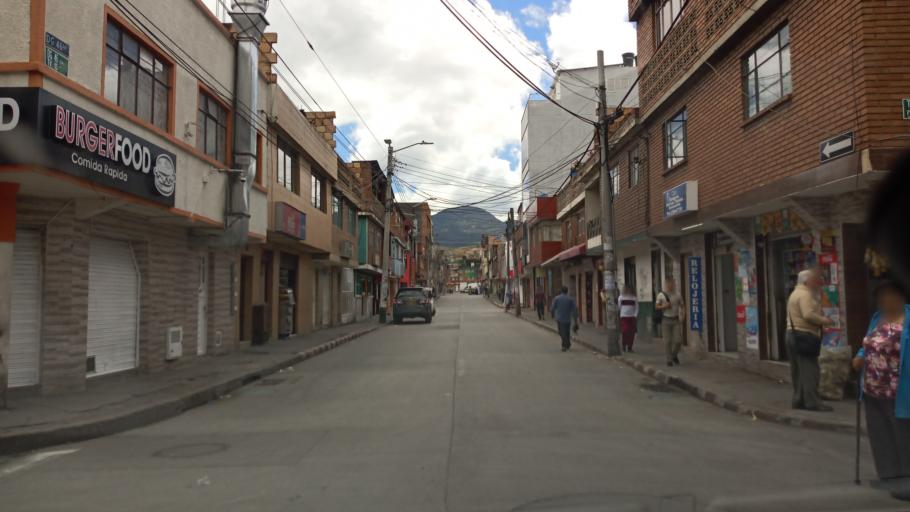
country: CO
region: Bogota D.C.
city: Bogota
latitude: 4.5694
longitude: -74.1238
